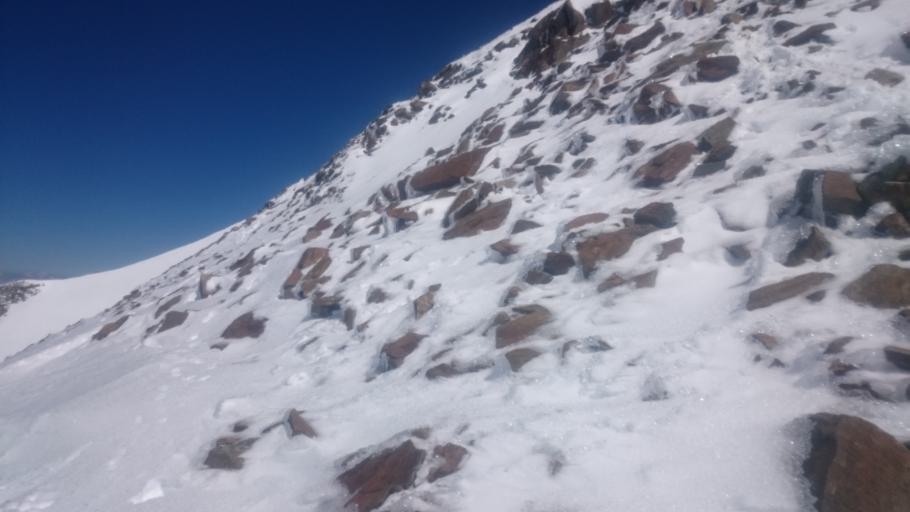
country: AT
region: Tyrol
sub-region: Politischer Bezirk Imst
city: Soelden
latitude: 46.8844
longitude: 10.8655
